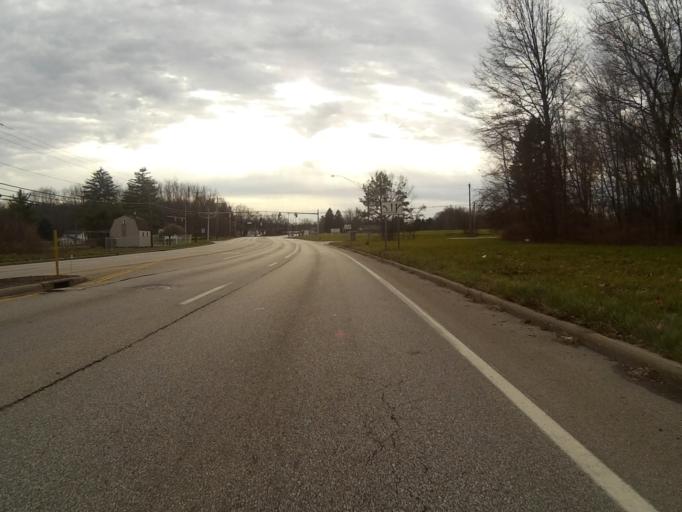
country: US
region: Ohio
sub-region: Portage County
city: Kent
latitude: 41.1308
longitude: -81.3519
